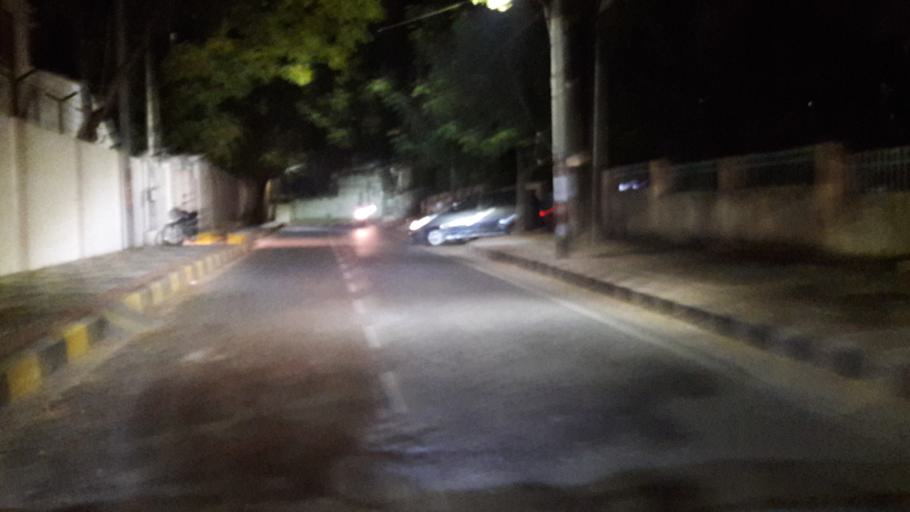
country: IN
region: Telangana
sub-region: Hyderabad
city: Hyderabad
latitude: 17.4356
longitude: 78.4593
